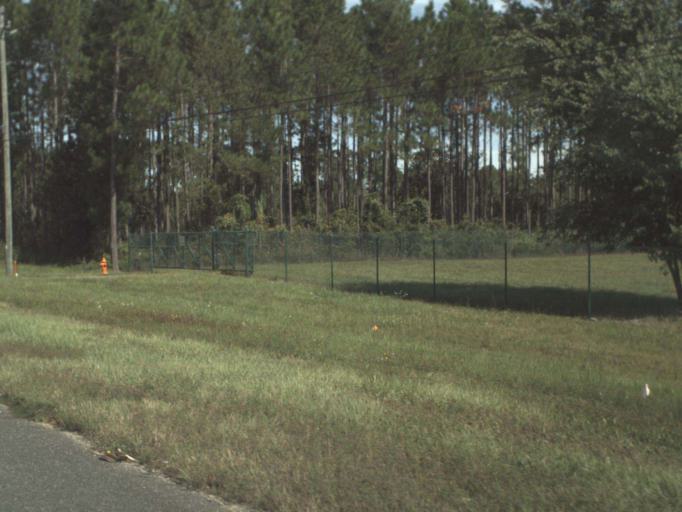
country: US
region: Florida
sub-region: Bay County
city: Lynn Haven
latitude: 30.3156
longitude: -85.6554
